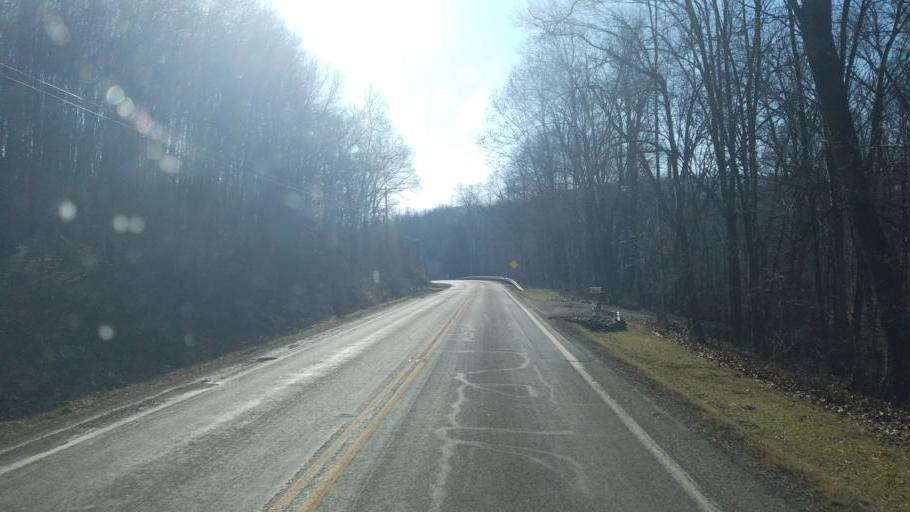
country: US
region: Ohio
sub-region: Ashland County
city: Loudonville
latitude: 40.6263
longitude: -82.1988
